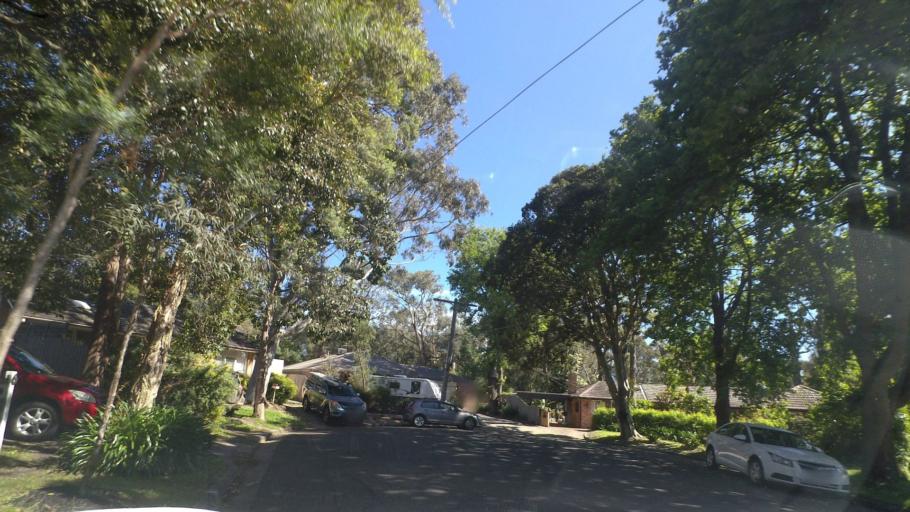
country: AU
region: Victoria
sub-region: Maroondah
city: Ringwood East
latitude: -37.8166
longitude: 145.2552
